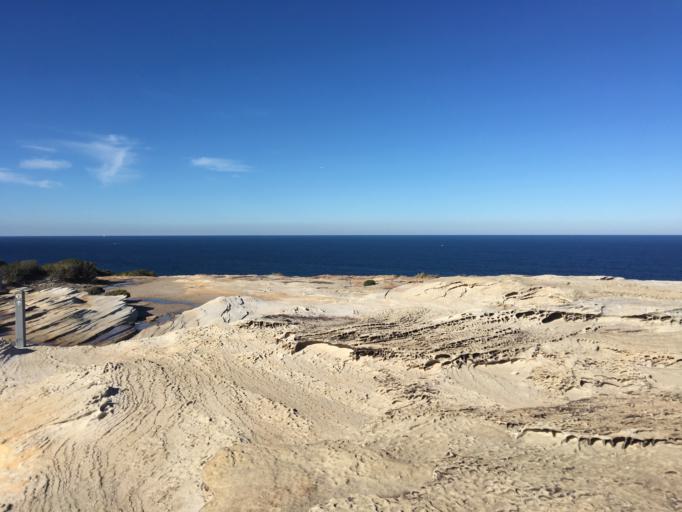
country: AU
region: New South Wales
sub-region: Sutherland Shire
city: Bundeena
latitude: -34.1289
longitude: 151.1307
